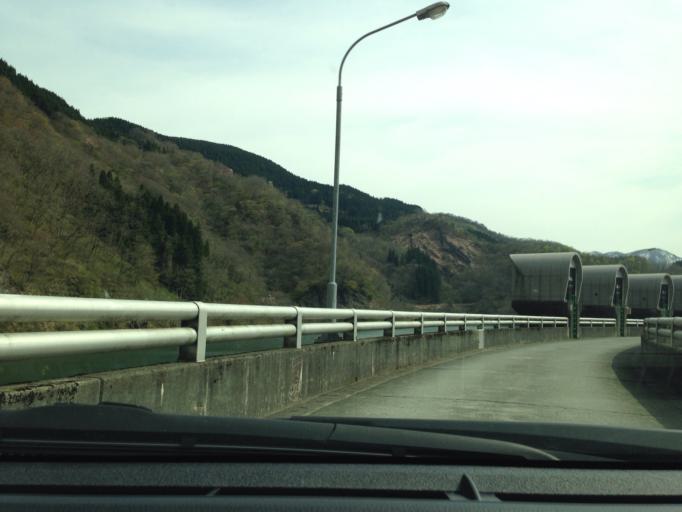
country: JP
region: Toyama
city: Fukumitsu
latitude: 36.4707
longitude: 136.8065
